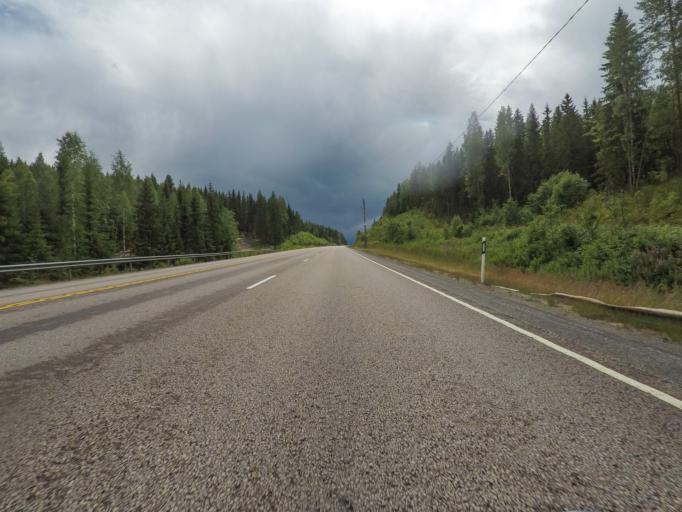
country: FI
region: Central Finland
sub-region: Jyvaeskylae
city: Toivakka
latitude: 62.0521
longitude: 26.0518
